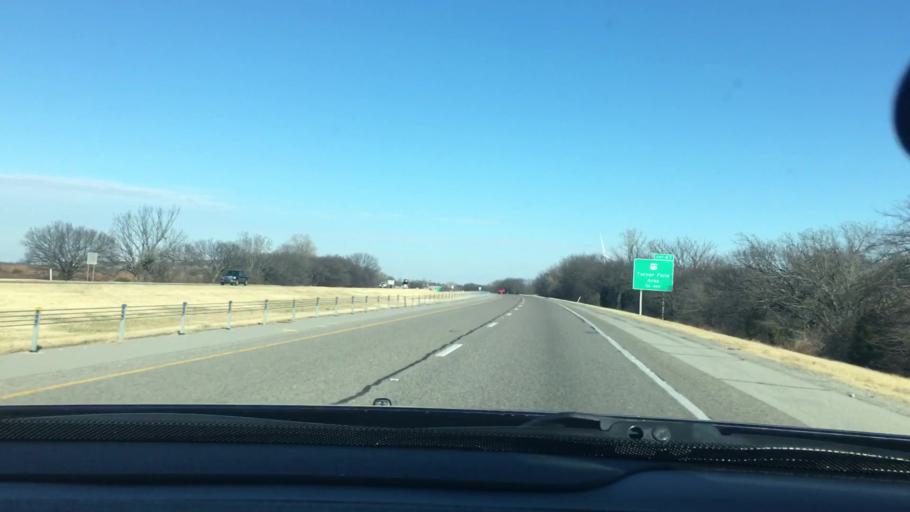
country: US
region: Oklahoma
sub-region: Murray County
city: Davis
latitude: 34.3835
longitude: -97.1421
